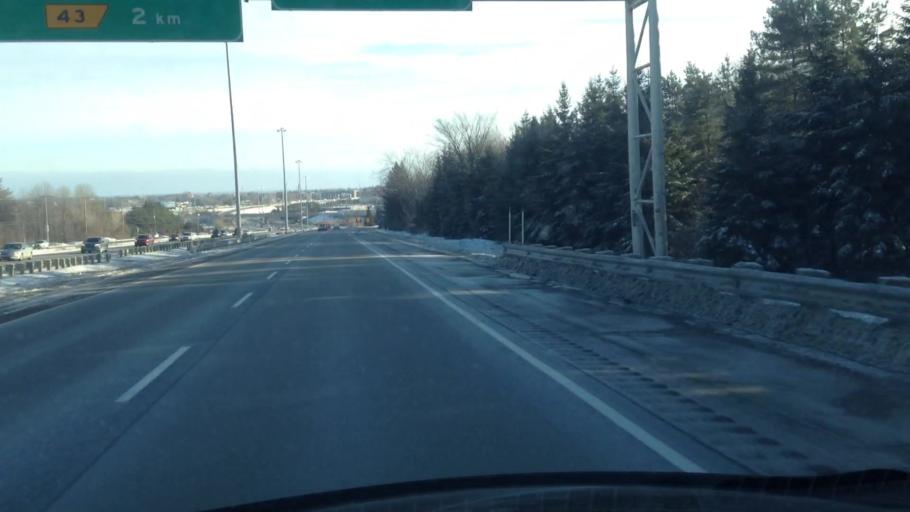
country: CA
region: Quebec
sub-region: Laurentides
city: Saint-Jerome
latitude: 45.8014
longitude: -74.0325
